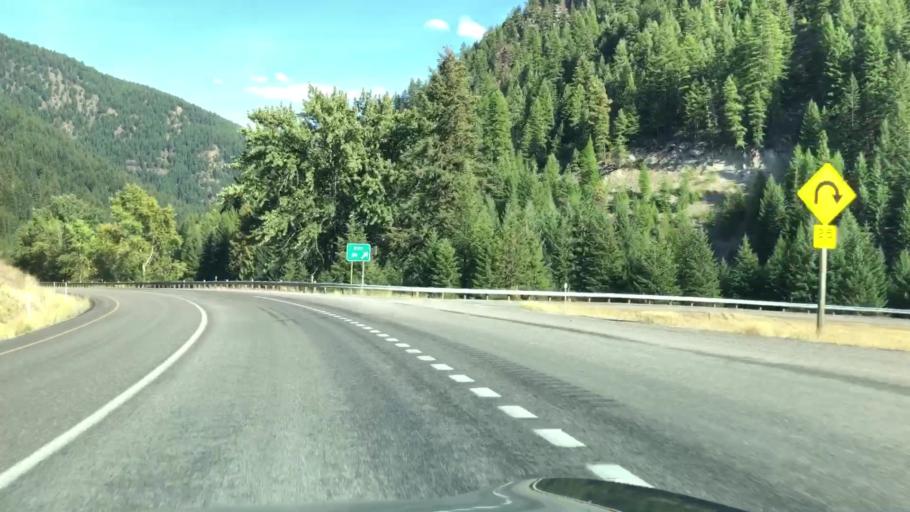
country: US
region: Montana
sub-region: Sanders County
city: Thompson Falls
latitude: 47.3127
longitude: -115.2331
